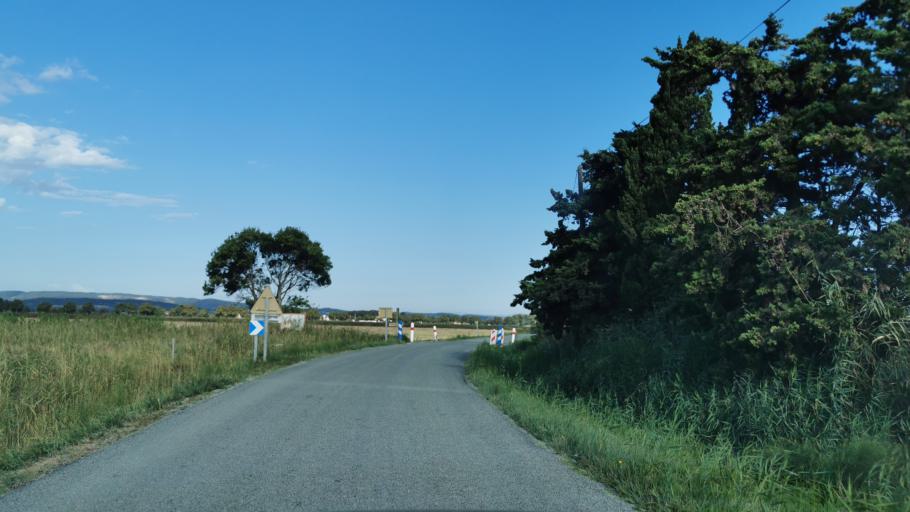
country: FR
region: Languedoc-Roussillon
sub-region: Departement de l'Aude
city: Gruissan
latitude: 43.1148
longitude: 3.0410
